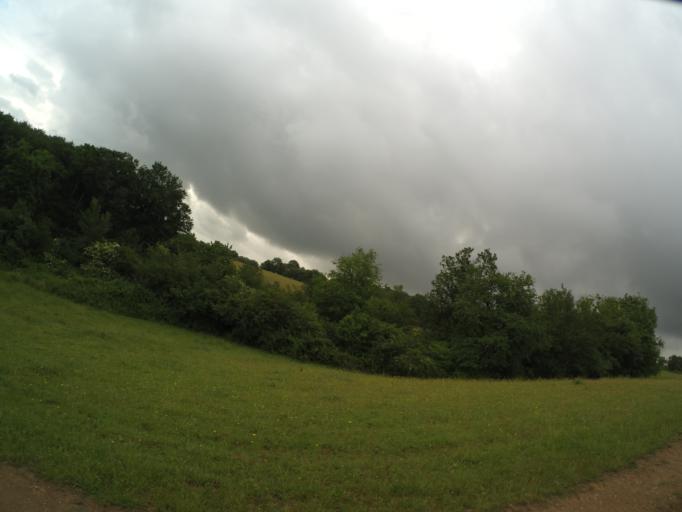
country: FR
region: Pays de la Loire
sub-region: Departement de la Vendee
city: Nesmy
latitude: 46.6045
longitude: -1.3747
